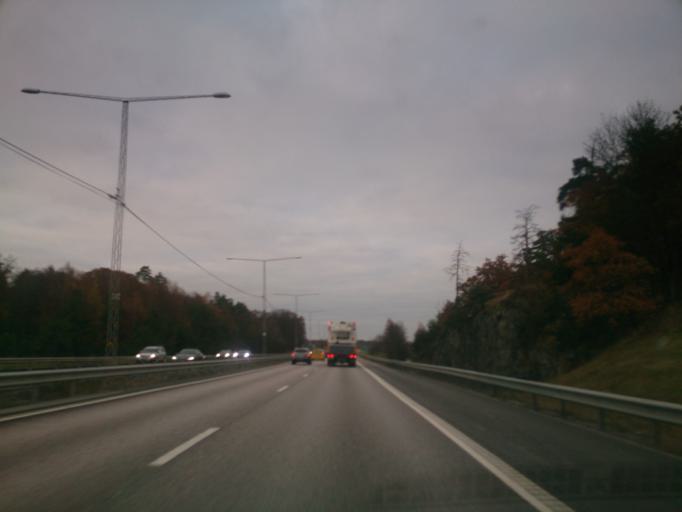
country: SE
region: Stockholm
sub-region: Sigtuna Kommun
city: Rosersberg
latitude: 59.5567
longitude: 17.8984
